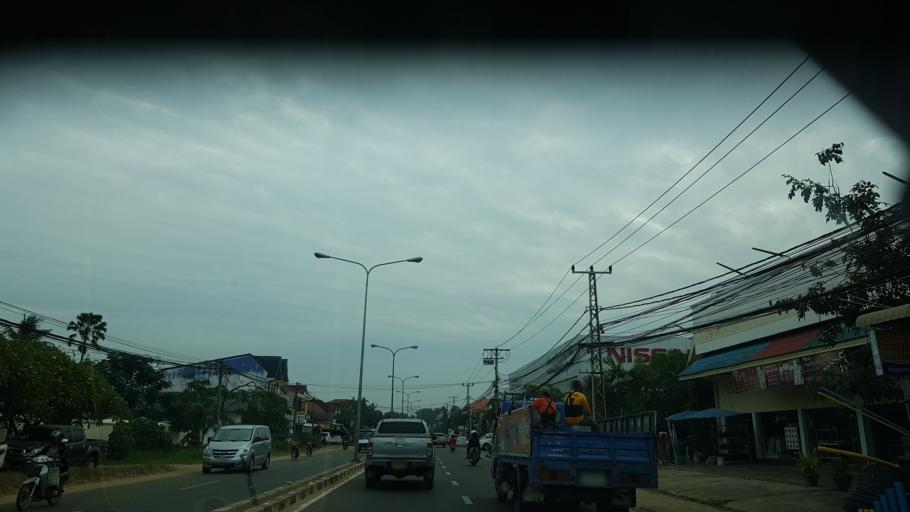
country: TH
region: Nong Khai
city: Si Chiang Mai
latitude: 17.9171
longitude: 102.6197
